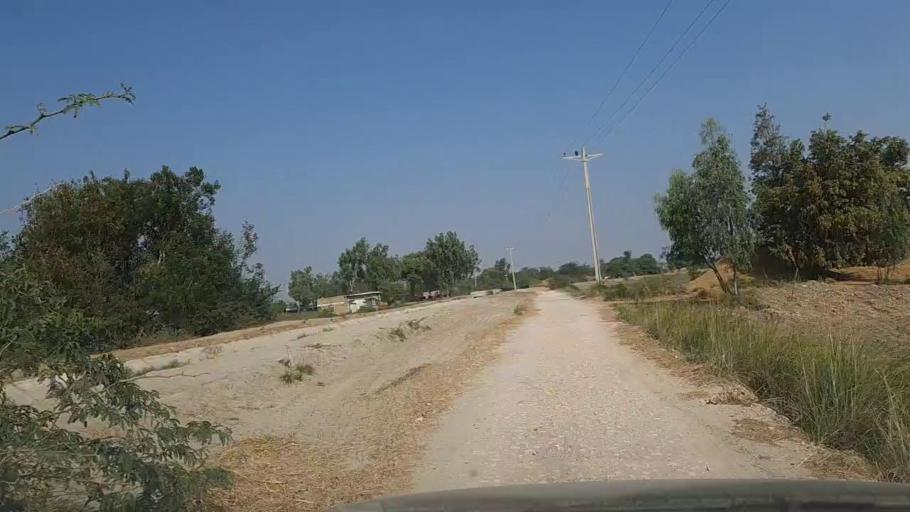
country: PK
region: Sindh
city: Mirpur Sakro
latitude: 24.5177
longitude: 67.8054
